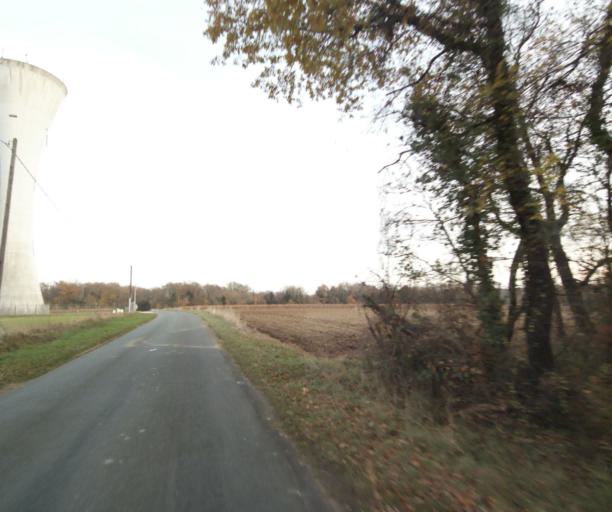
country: FR
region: Poitou-Charentes
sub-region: Departement de la Charente-Maritime
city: Fontcouverte
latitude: 45.7991
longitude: -0.5737
